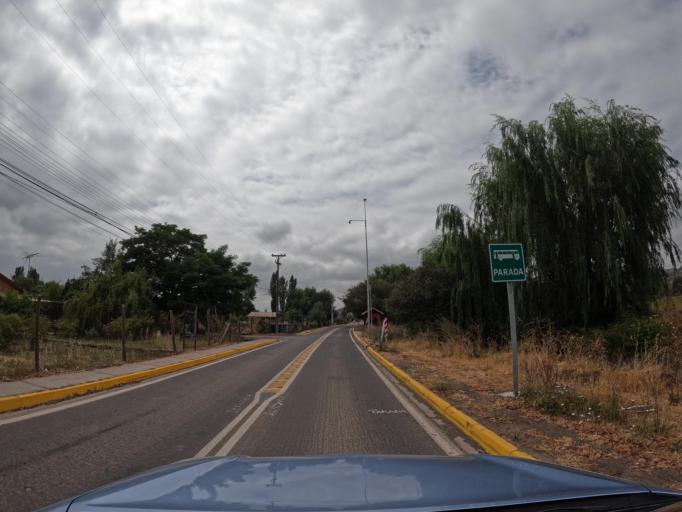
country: CL
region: Maule
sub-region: Provincia de Curico
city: Teno
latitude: -34.7715
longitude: -71.1878
